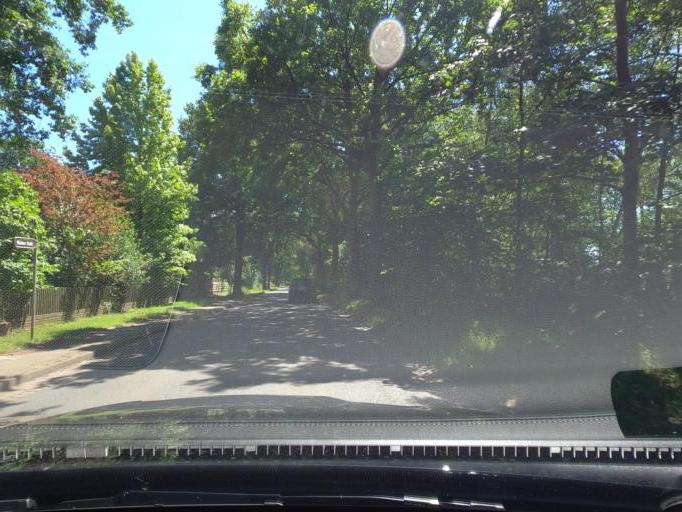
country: DE
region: Lower Saxony
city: Hohne
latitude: 52.5841
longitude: 10.3750
